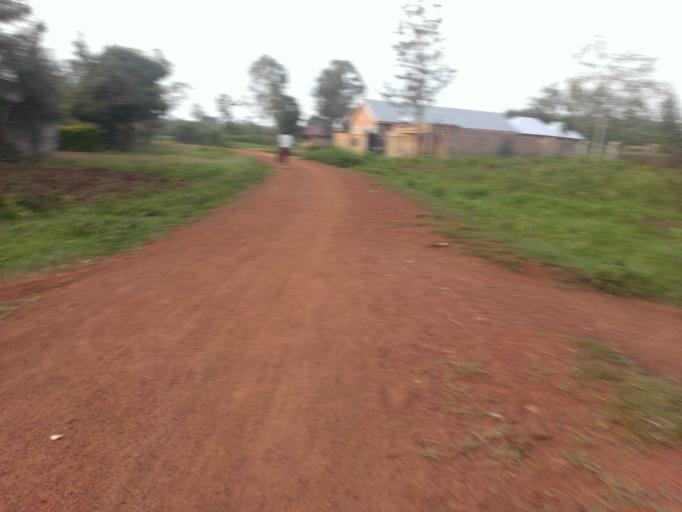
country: UG
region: Eastern Region
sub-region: Busia District
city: Busia
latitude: 0.5480
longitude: 34.0450
